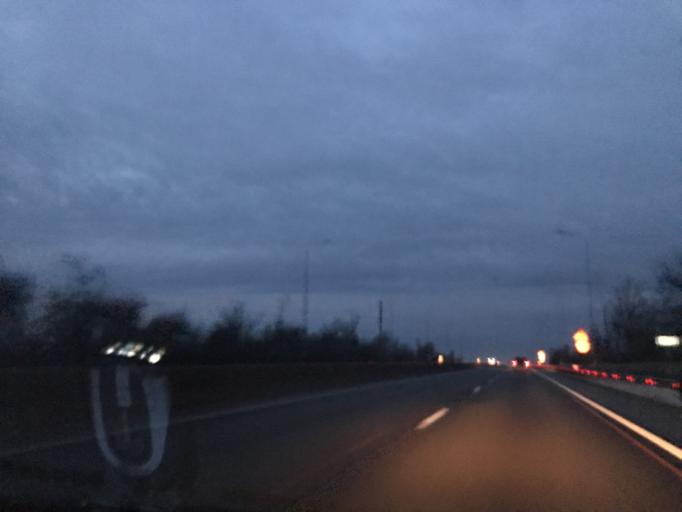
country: RU
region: Rostov
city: Samarskoye
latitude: 47.0204
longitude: 39.7362
